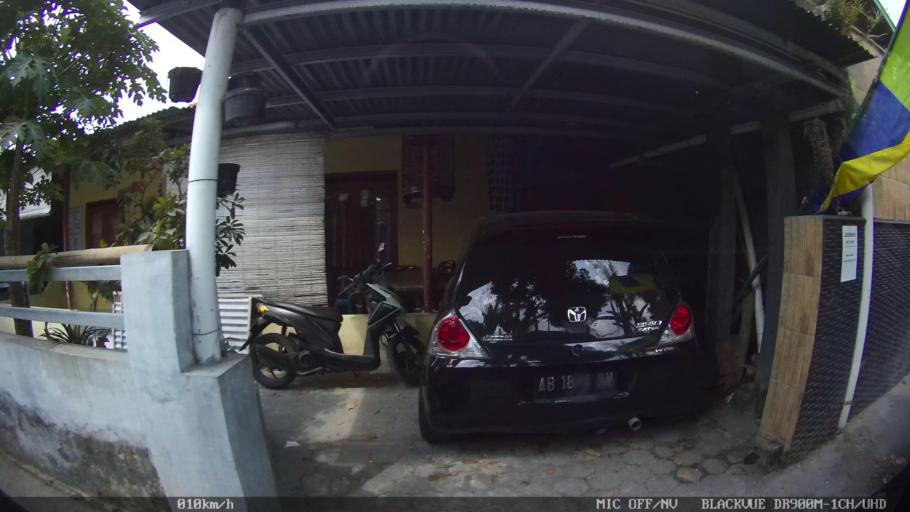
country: ID
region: Daerah Istimewa Yogyakarta
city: Depok
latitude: -7.8022
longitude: 110.4076
